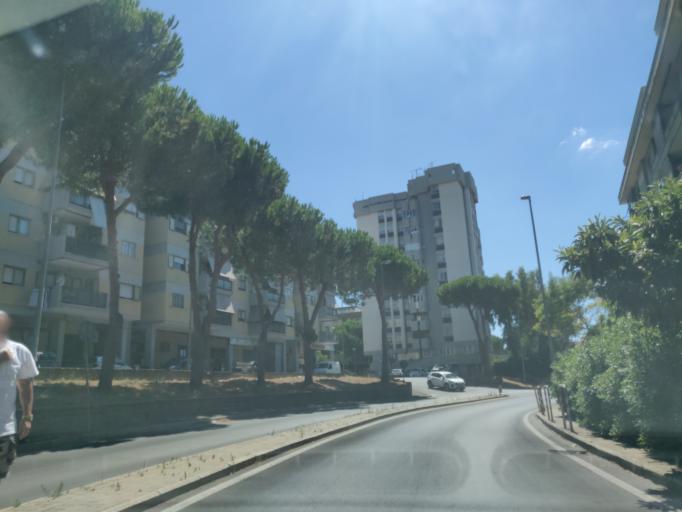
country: IT
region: Latium
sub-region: Citta metropolitana di Roma Capitale
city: Civitavecchia
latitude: 42.0820
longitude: 11.8133
